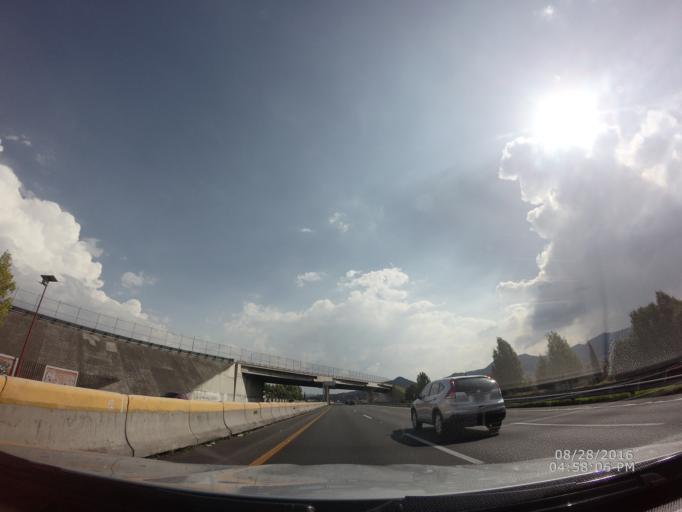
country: MX
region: Mexico
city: Ecatepec
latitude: 19.6102
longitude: -99.0342
